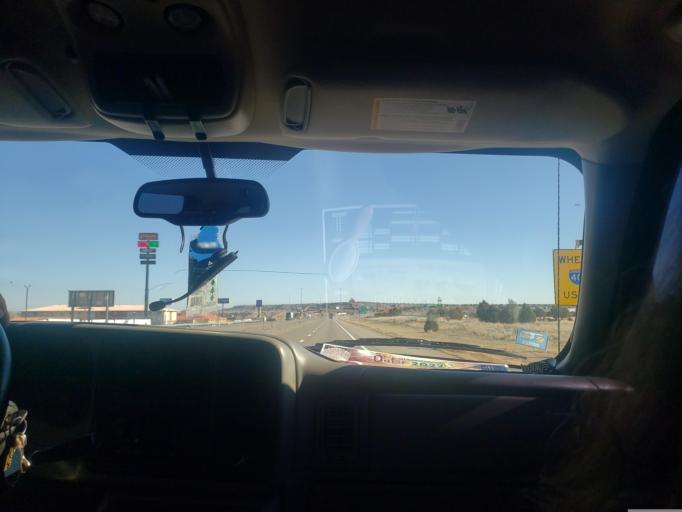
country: US
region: New Mexico
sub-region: Guadalupe County
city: Santa Rosa
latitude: 34.9448
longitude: -104.6508
